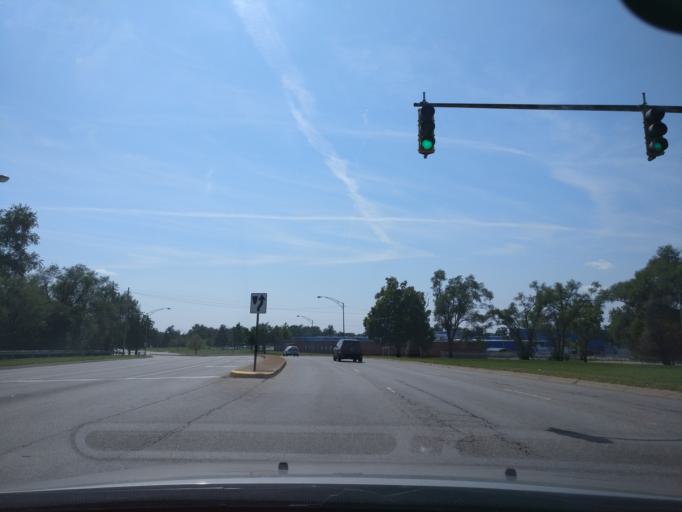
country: US
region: Ohio
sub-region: Butler County
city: Middletown
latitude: 39.5013
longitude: -84.3965
